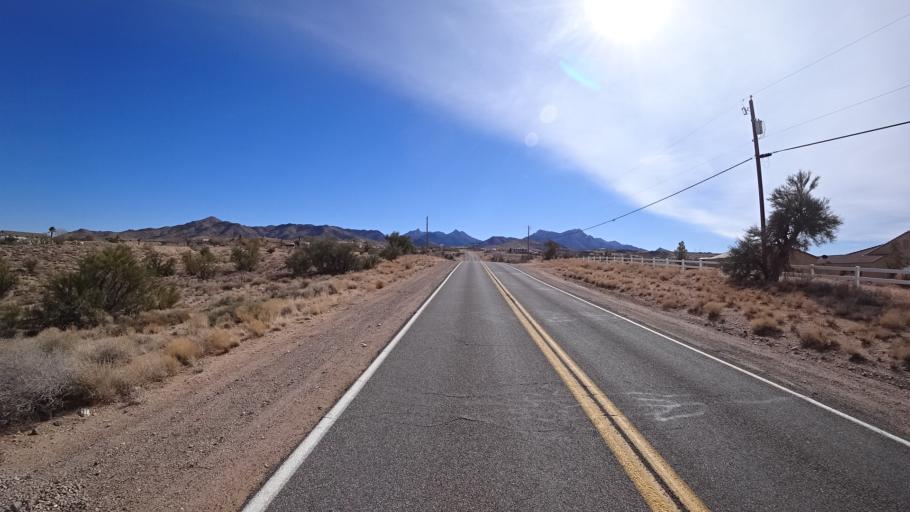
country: US
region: Arizona
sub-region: Mohave County
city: Kingman
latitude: 35.1720
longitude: -113.9824
